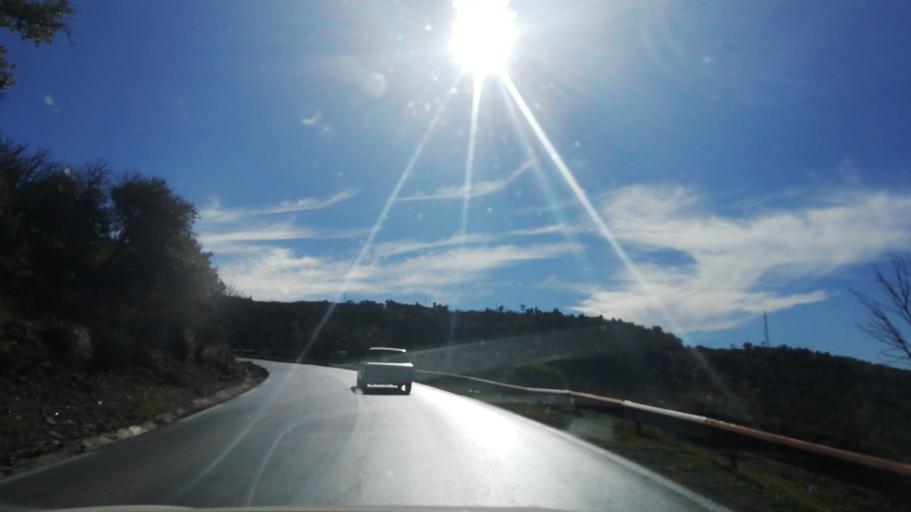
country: DZ
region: Tlemcen
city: Mansoura
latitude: 34.8413
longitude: -1.3689
